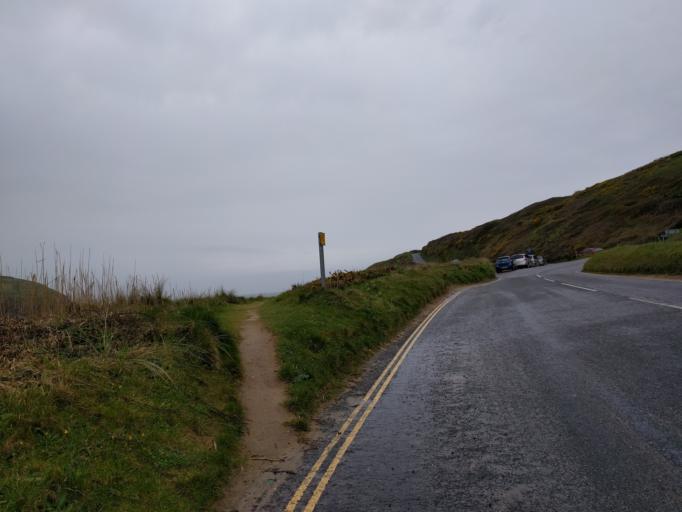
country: GB
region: England
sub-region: Cornwall
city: Mullion
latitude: 50.0346
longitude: -5.2601
